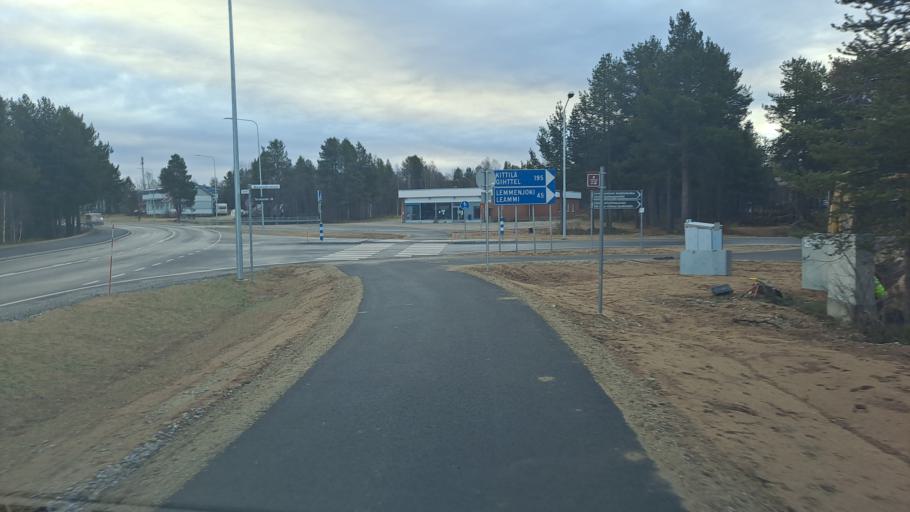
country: FI
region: Lapland
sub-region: Pohjois-Lappi
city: Inari
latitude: 68.9072
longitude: 27.0150
